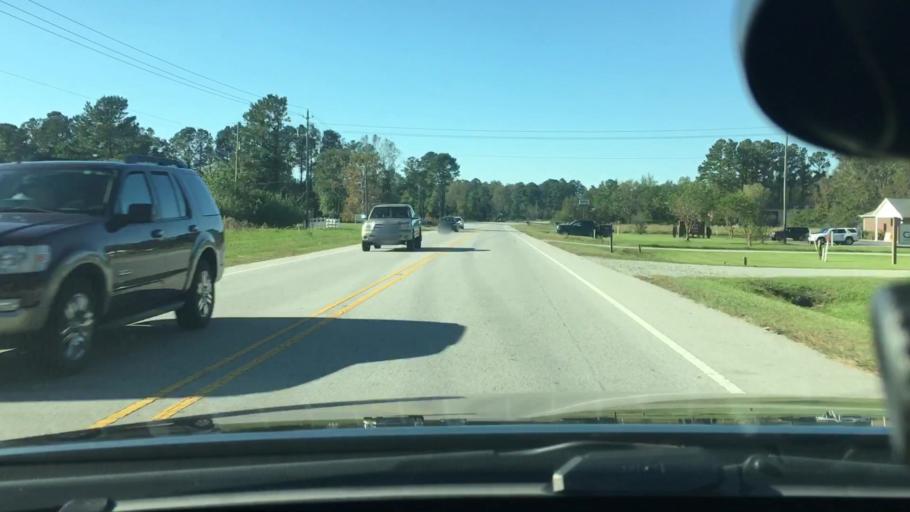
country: US
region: North Carolina
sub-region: Craven County
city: Trent Woods
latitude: 35.1584
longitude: -77.1153
